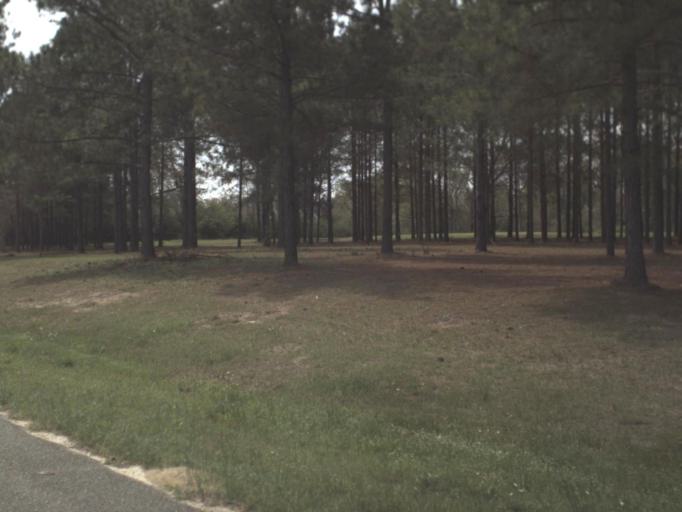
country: US
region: Florida
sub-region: Jackson County
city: Graceville
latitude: 30.8930
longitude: -85.5237
